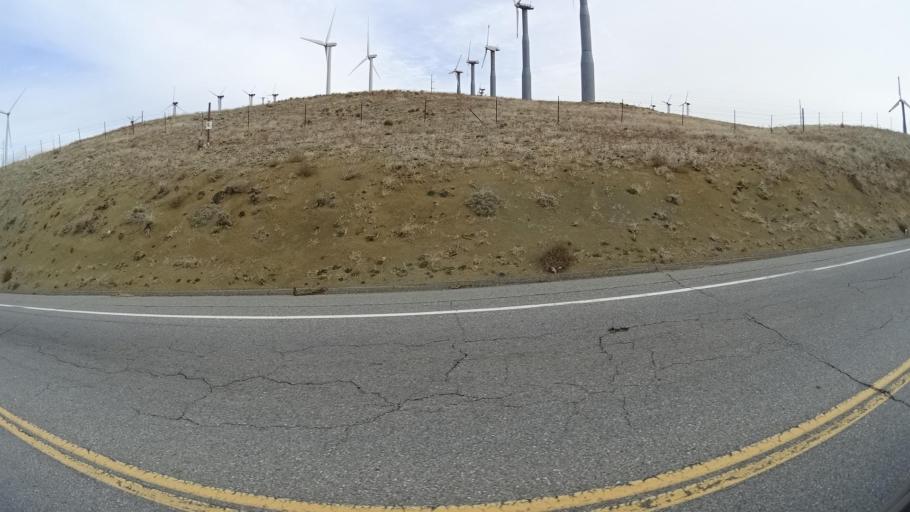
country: US
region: California
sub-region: Kern County
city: Tehachapi
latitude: 35.0622
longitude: -118.3900
